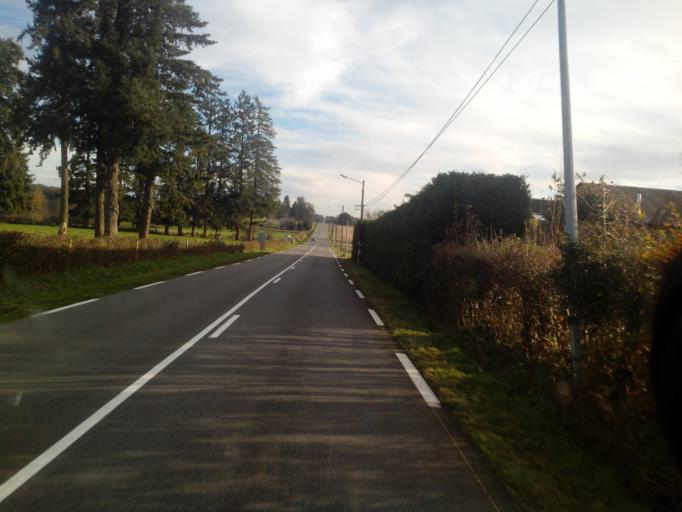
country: FR
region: Limousin
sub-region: Departement de la Haute-Vienne
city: Neuvic-Entier
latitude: 45.7577
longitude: 1.5908
